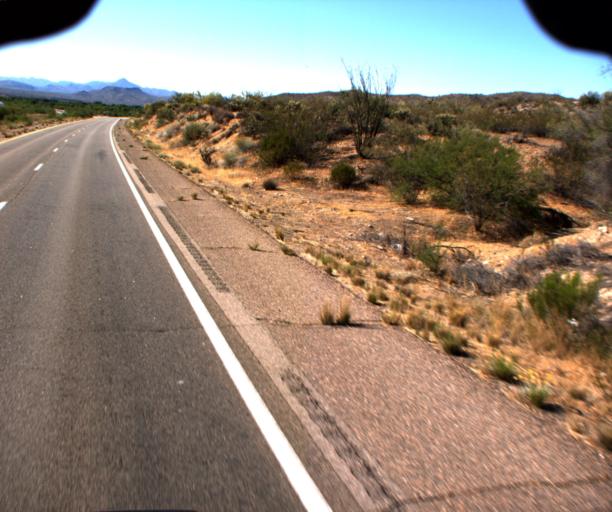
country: US
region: Arizona
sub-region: Yavapai County
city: Bagdad
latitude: 34.6737
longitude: -113.5897
